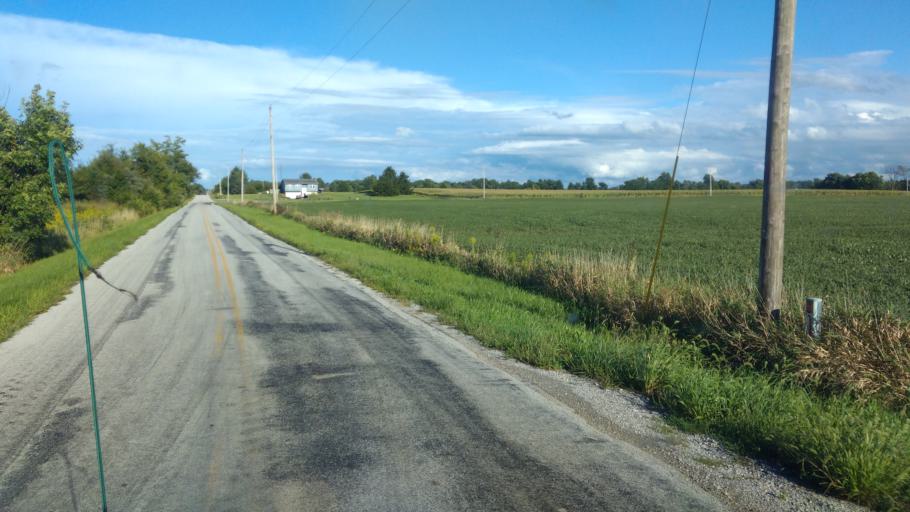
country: US
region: Ohio
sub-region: Hardin County
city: Forest
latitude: 40.7531
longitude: -83.6046
